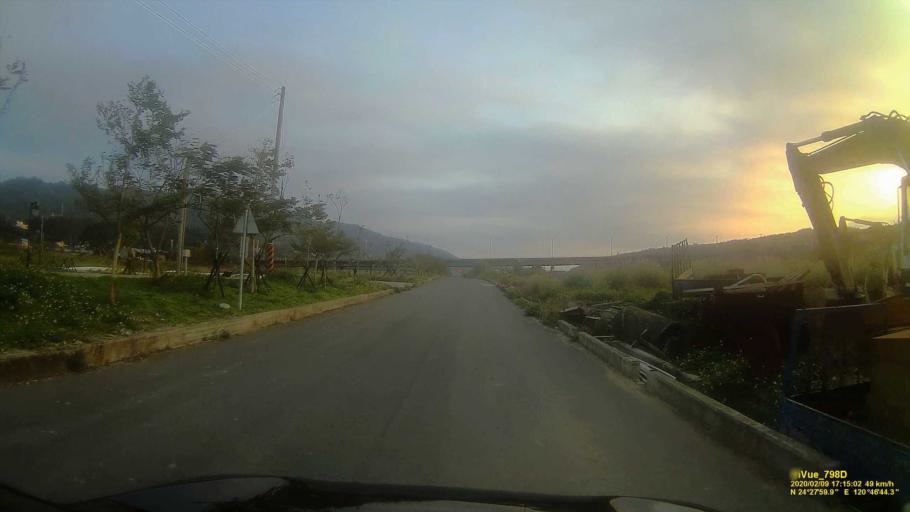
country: TW
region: Taiwan
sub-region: Miaoli
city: Miaoli
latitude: 24.4662
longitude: 120.7787
